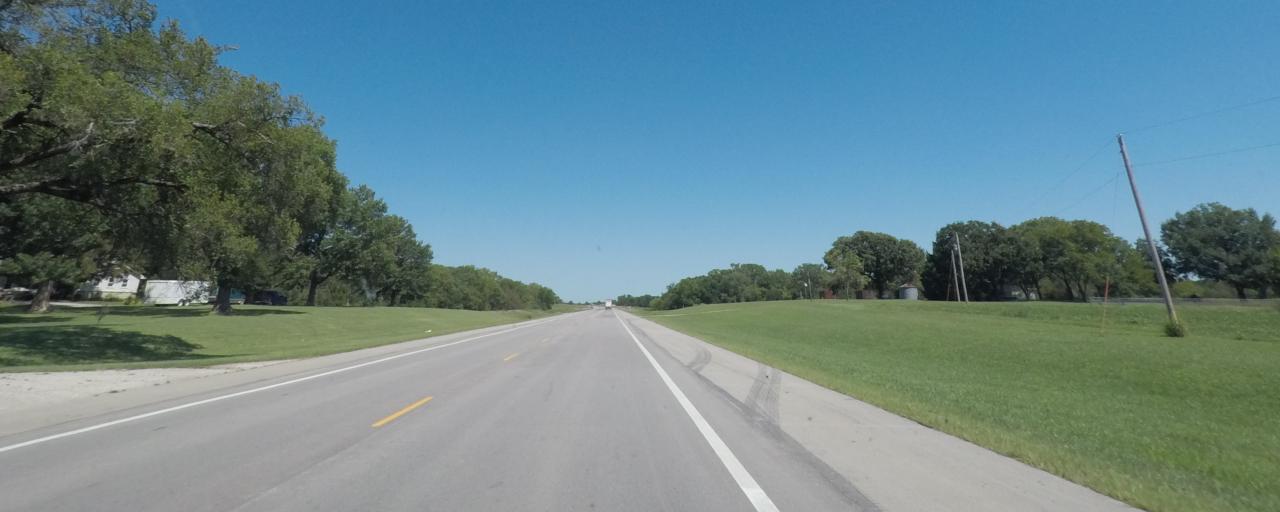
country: US
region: Kansas
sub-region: Lyon County
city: Emporia
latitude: 38.4080
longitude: -96.2991
